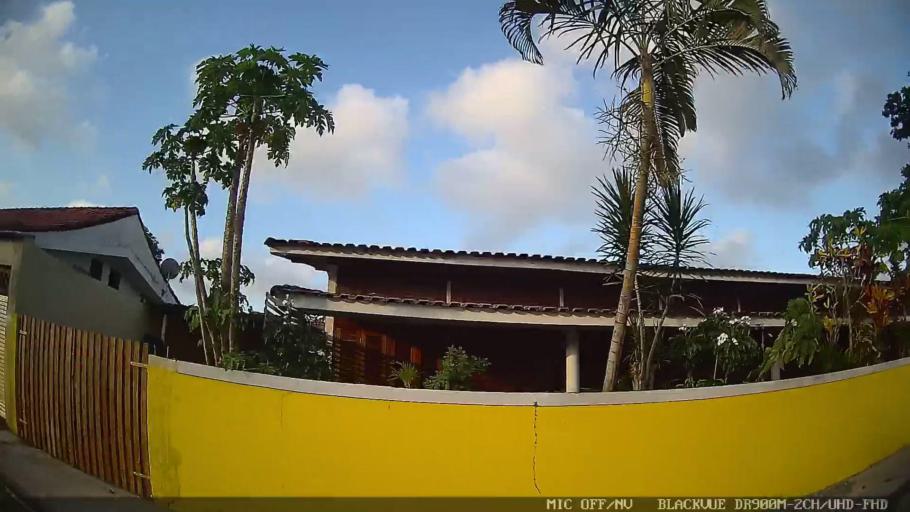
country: BR
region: Sao Paulo
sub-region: Peruibe
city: Peruibe
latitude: -24.3192
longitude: -46.9906
